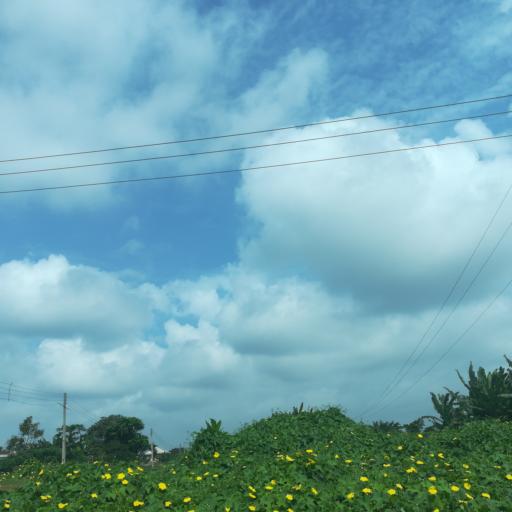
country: NG
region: Lagos
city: Ikorodu
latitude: 6.6604
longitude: 3.6804
